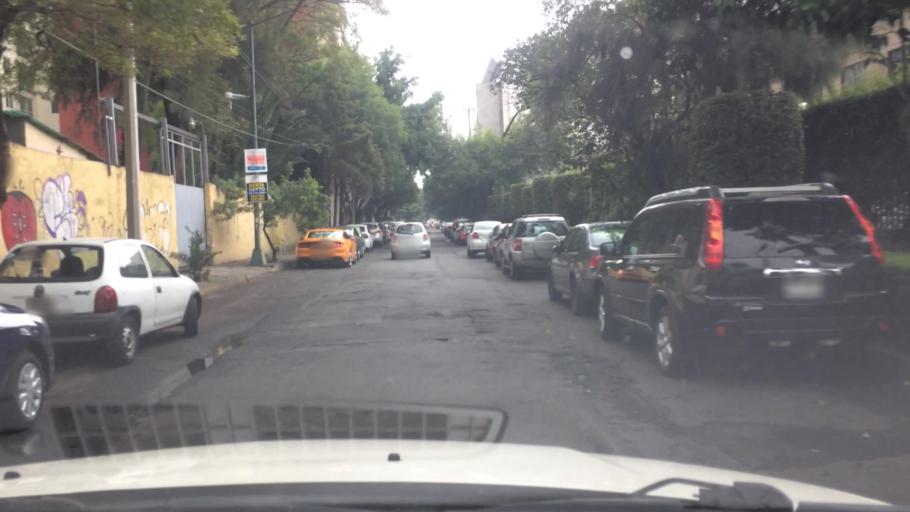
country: MX
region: Mexico City
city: Colonia del Valle
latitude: 19.3750
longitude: -99.1711
